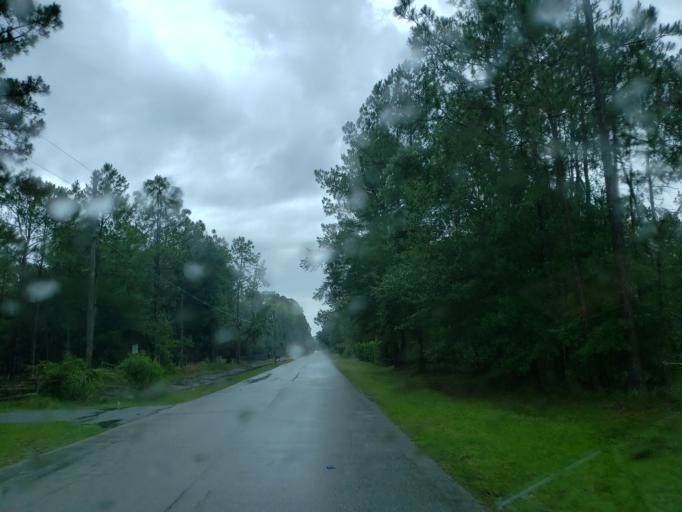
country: US
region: Florida
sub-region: Pasco County
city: Wesley Chapel
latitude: 28.2730
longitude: -82.3607
